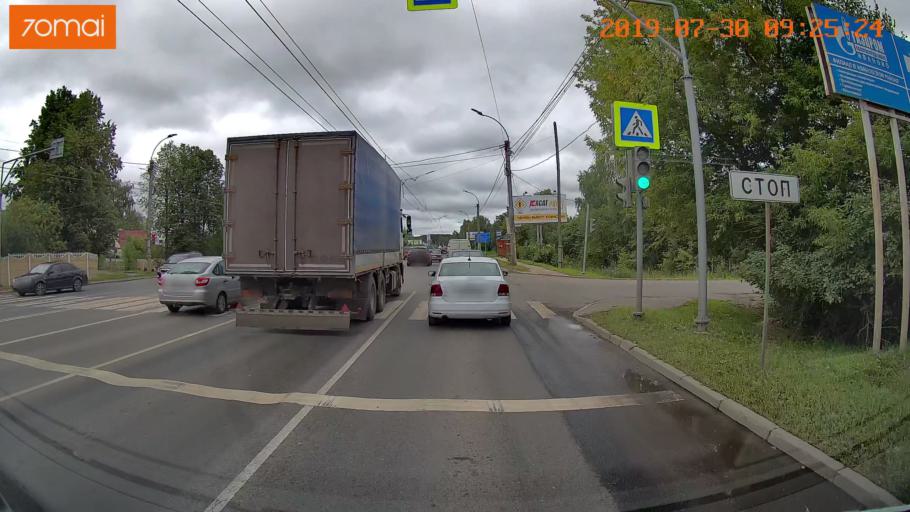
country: RU
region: Ivanovo
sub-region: Gorod Ivanovo
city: Ivanovo
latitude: 56.9529
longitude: 40.9747
